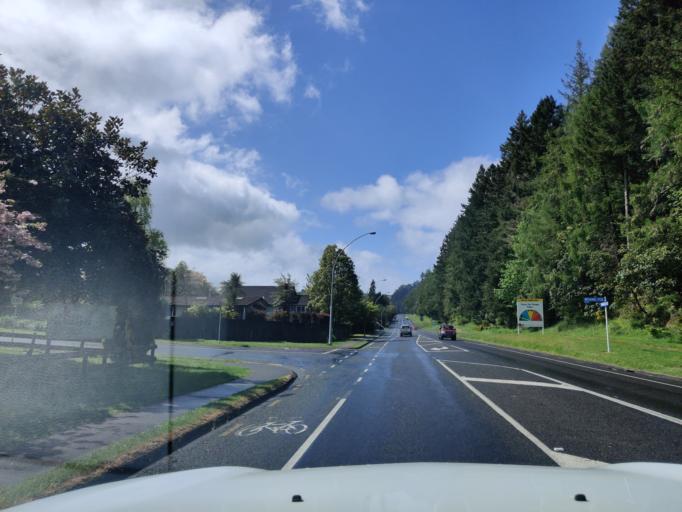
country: NZ
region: Bay of Plenty
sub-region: Rotorua District
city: Rotorua
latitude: -38.1503
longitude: 176.2813
